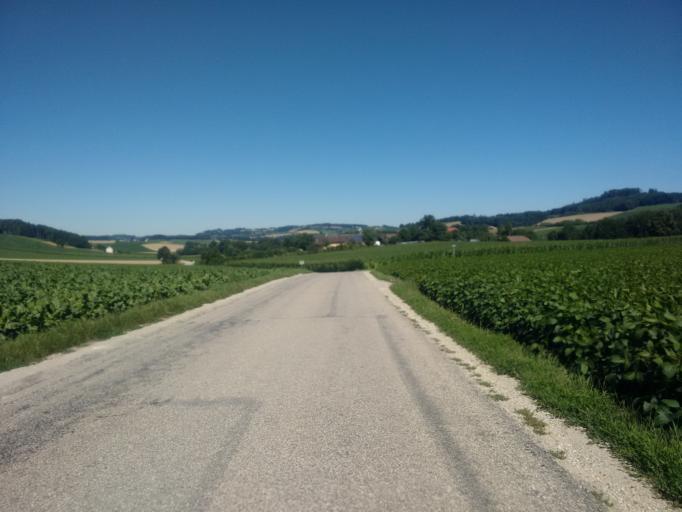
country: AT
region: Upper Austria
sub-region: Wels-Land
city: Buchkirchen
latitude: 48.2194
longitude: 13.9965
